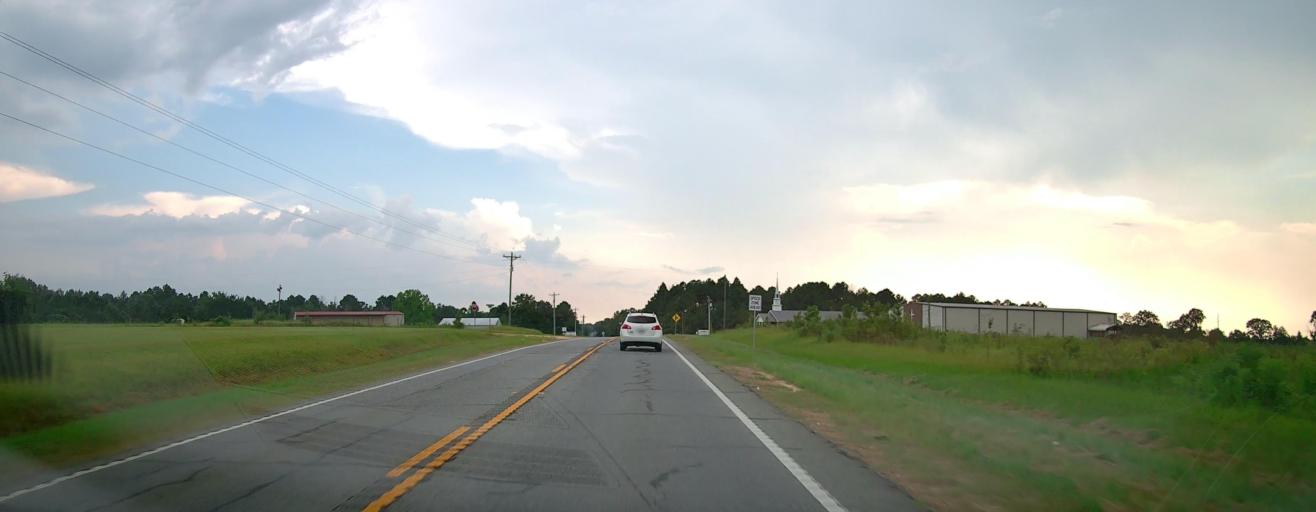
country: US
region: Georgia
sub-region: Laurens County
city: East Dublin
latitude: 32.5663
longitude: -82.8469
